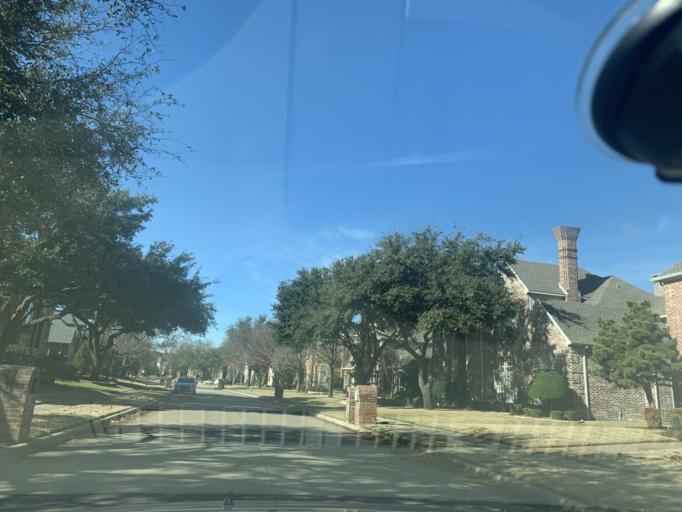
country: US
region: Texas
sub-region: Denton County
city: The Colony
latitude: 33.0526
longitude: -96.8175
